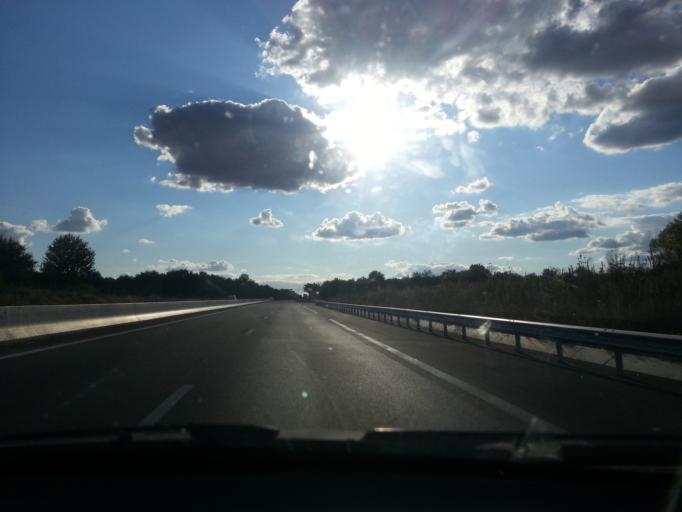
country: FR
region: Bourgogne
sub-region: Departement de Saone-et-Loire
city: Saint-Remy
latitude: 46.7556
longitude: 4.8120
